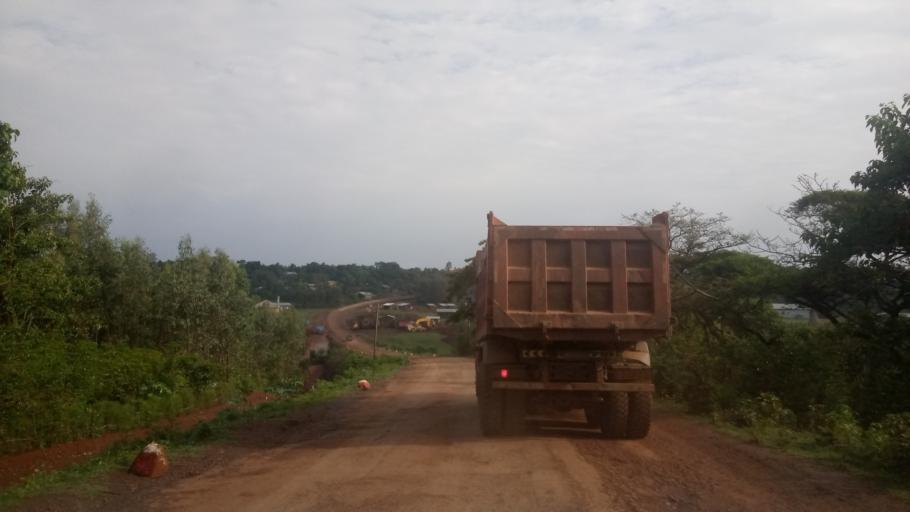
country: ET
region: Oromiya
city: Agaro
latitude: 7.8549
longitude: 36.6541
